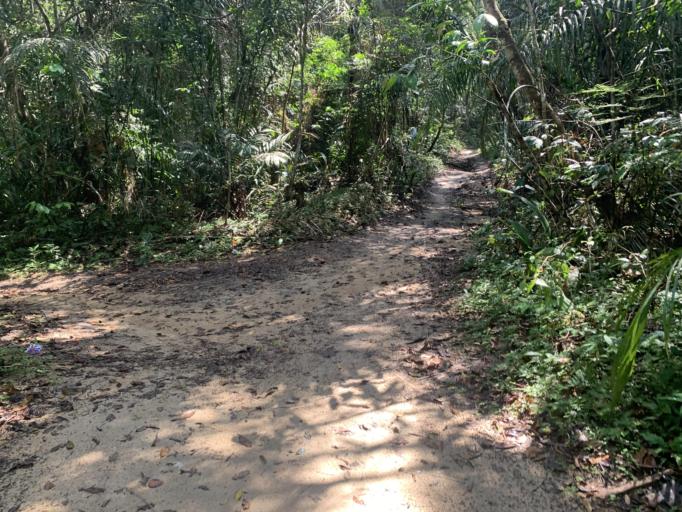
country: BR
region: Amazonas
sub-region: Manaus
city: Manaus
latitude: -3.0968
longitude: -59.9543
